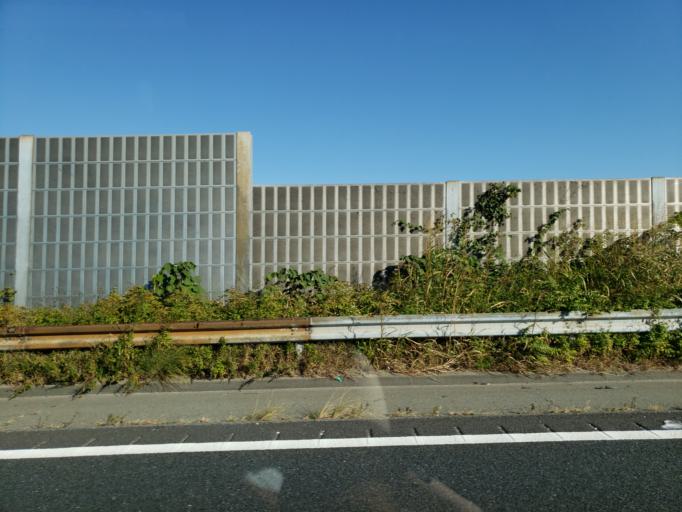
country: JP
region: Hyogo
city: Kakogawacho-honmachi
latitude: 34.7166
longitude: 134.9092
